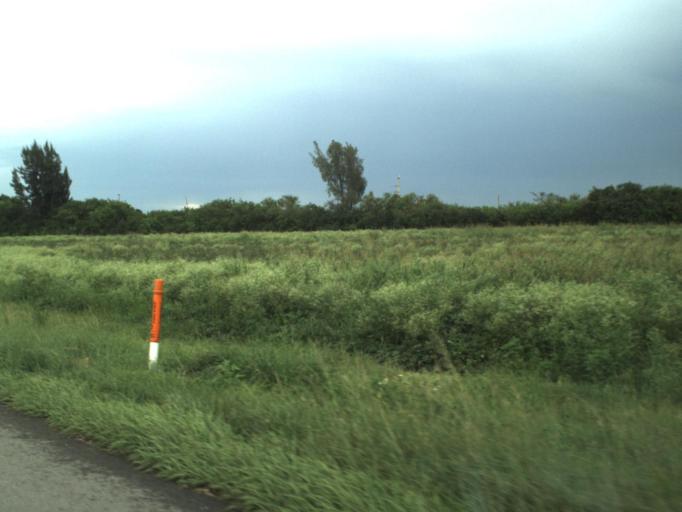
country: US
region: Florida
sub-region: Miami-Dade County
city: The Hammocks
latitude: 25.6769
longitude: -80.4808
